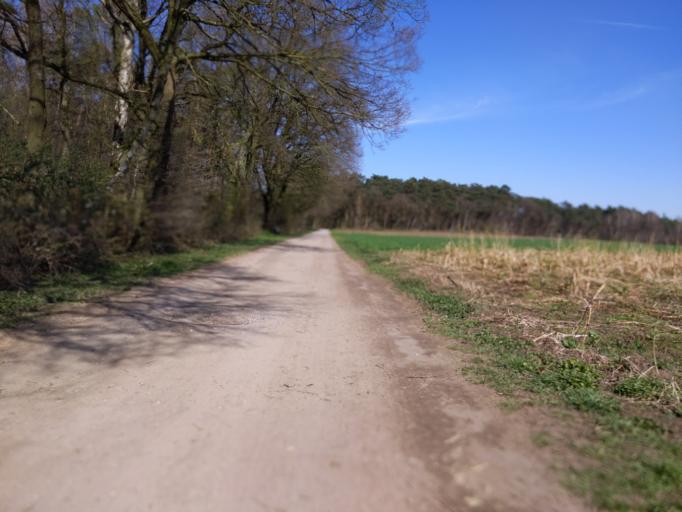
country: DE
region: North Rhine-Westphalia
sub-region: Regierungsbezirk Dusseldorf
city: Schermbeck
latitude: 51.7011
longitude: 6.8914
